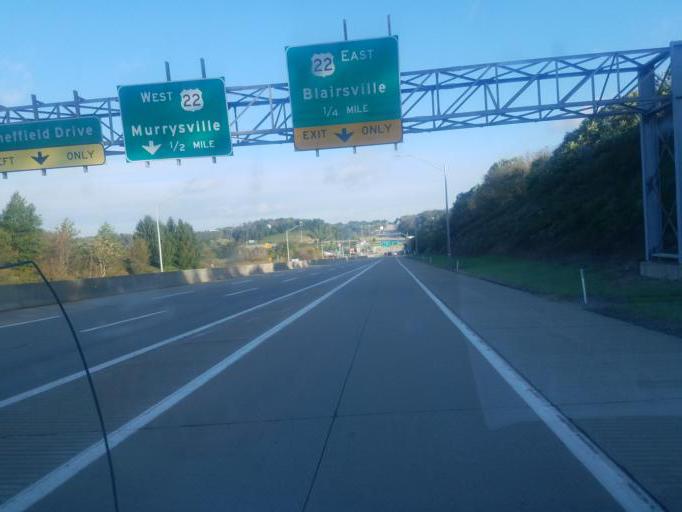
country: US
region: Pennsylvania
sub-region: Westmoreland County
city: Delmont
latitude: 40.3911
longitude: -79.5702
